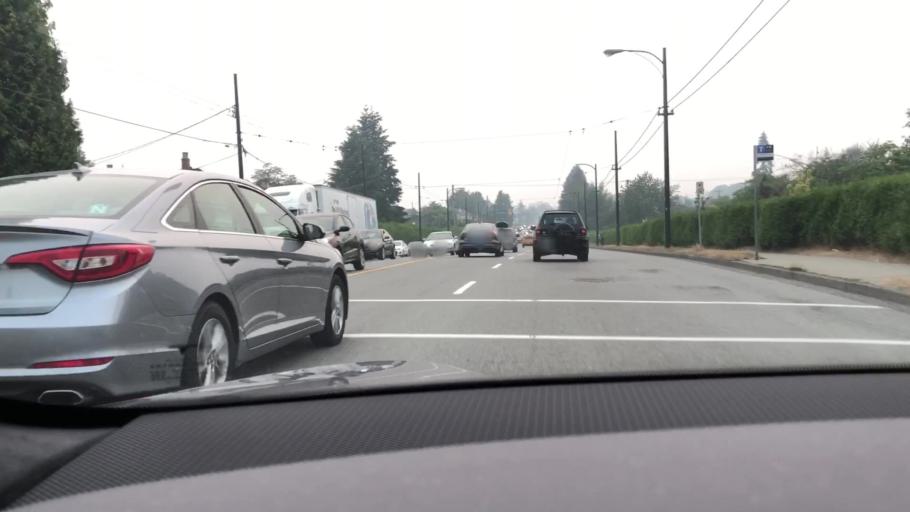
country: CA
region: British Columbia
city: Vancouver
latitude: 49.2330
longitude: -123.0946
